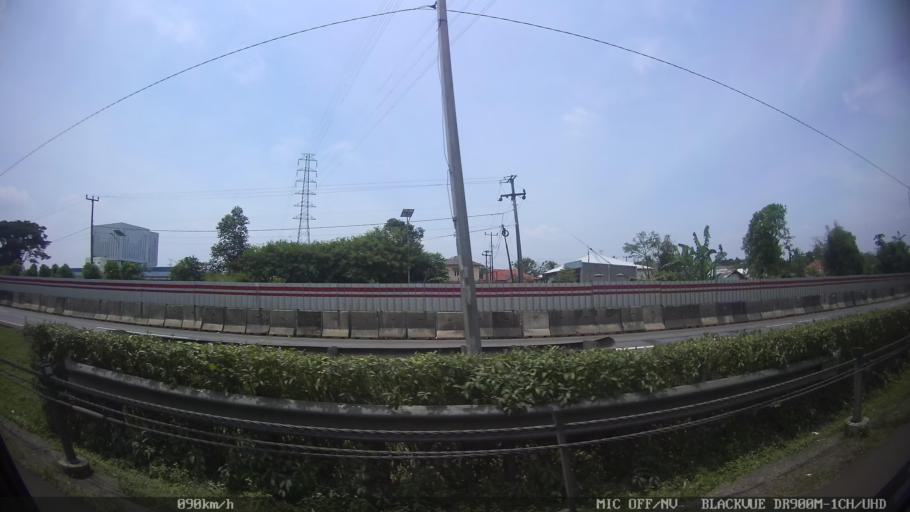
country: ID
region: West Java
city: Kresek
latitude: -6.1710
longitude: 106.3444
